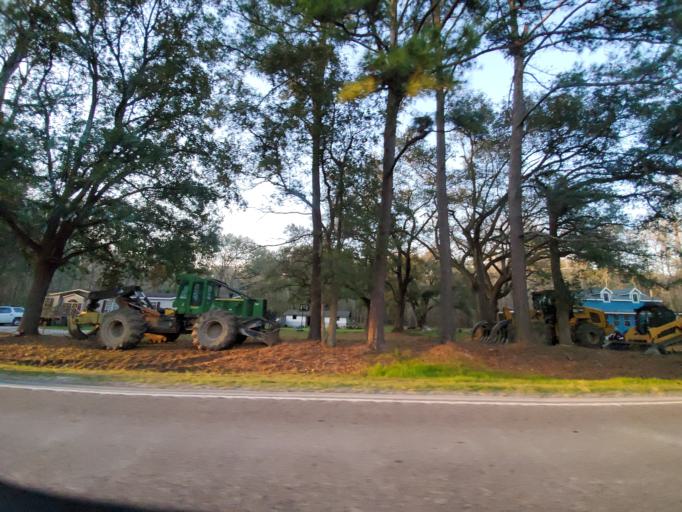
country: US
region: South Carolina
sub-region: Dorchester County
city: Ridgeville
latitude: 33.0229
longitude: -80.3753
